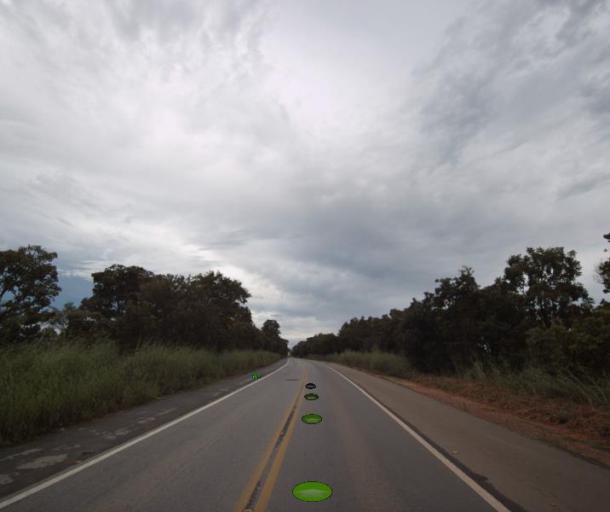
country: BR
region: Goias
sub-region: Porangatu
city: Porangatu
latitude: -13.4902
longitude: -49.1356
